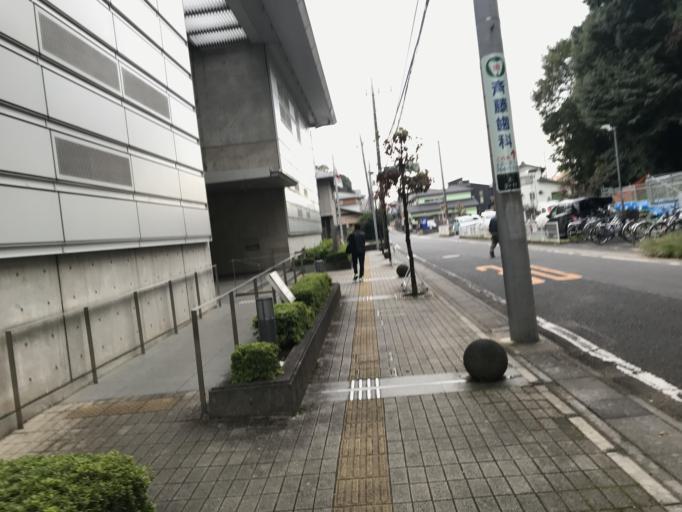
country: JP
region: Saitama
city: Hasuda
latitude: 35.9870
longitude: 139.6540
